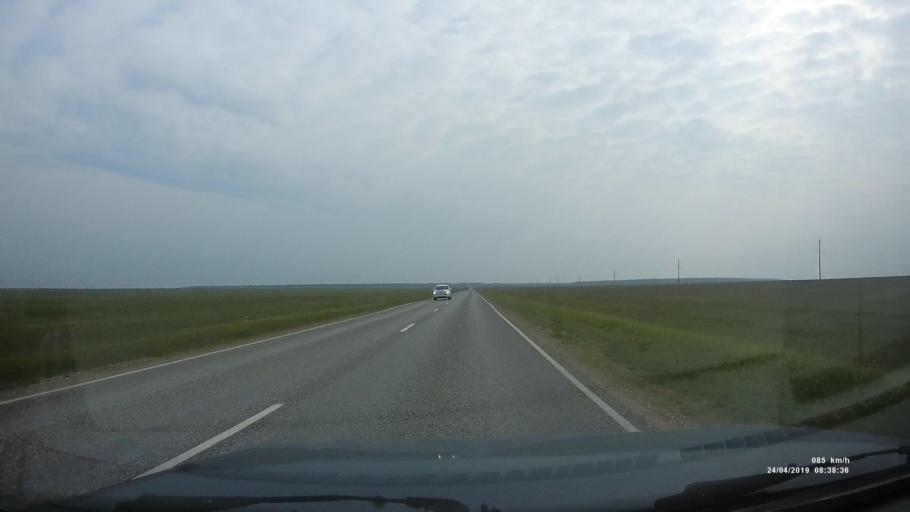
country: RU
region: Kalmykiya
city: Arshan'
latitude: 46.2163
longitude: 43.9700
